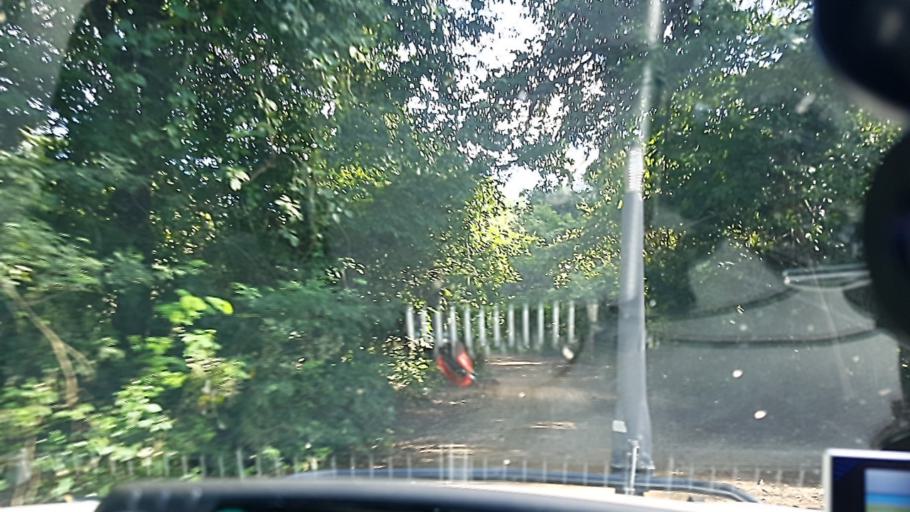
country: NI
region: Rivas
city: Tola
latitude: 11.5232
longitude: -86.1416
